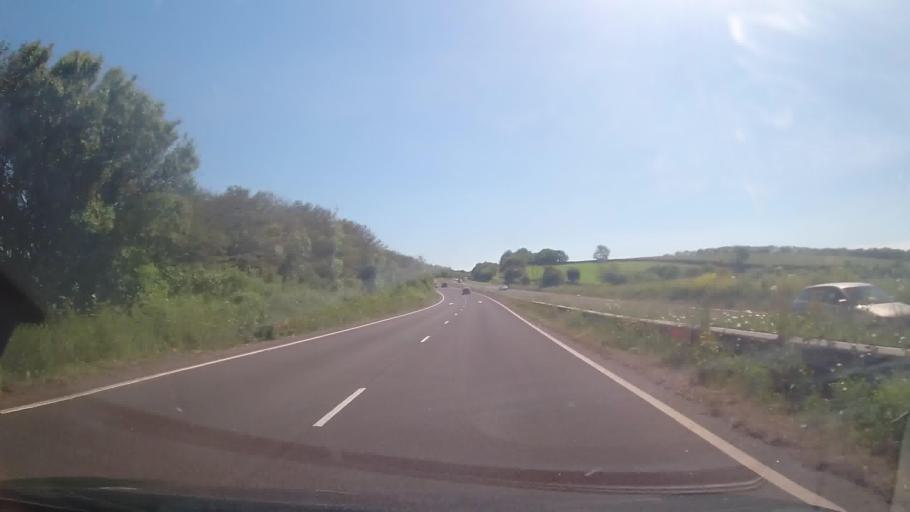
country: GB
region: England
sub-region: Devon
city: Marldon
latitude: 50.4675
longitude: -3.5828
